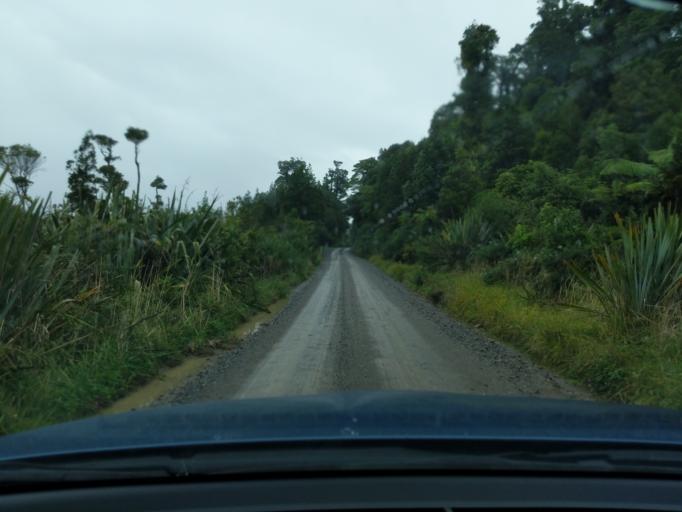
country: NZ
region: Tasman
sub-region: Tasman District
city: Takaka
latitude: -40.6431
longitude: 172.4809
